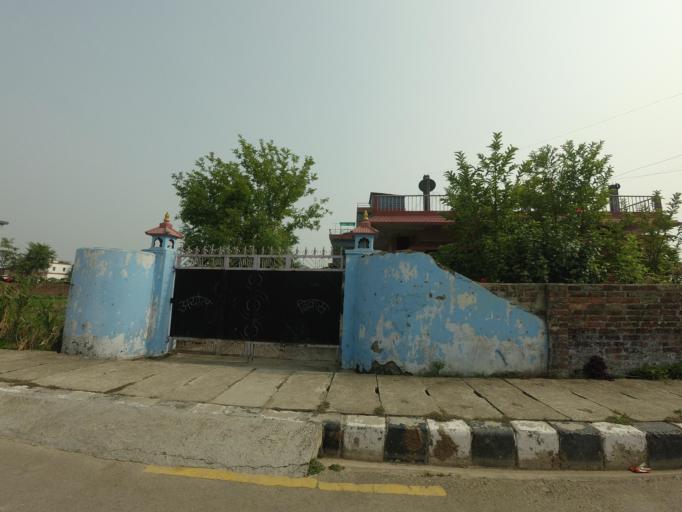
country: NP
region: Western Region
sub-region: Lumbini Zone
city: Bhairahawa
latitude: 27.5176
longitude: 83.4632
